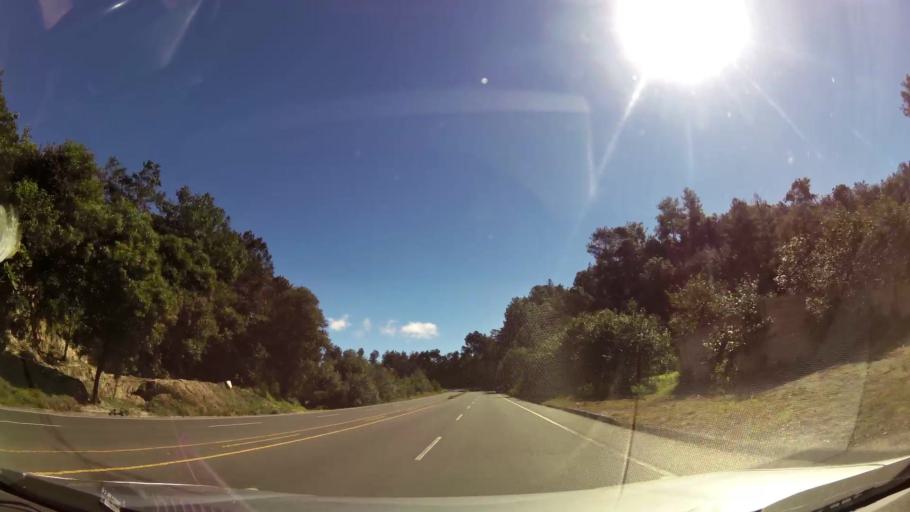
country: GT
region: Solola
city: Solola
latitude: 14.8149
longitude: -91.2053
